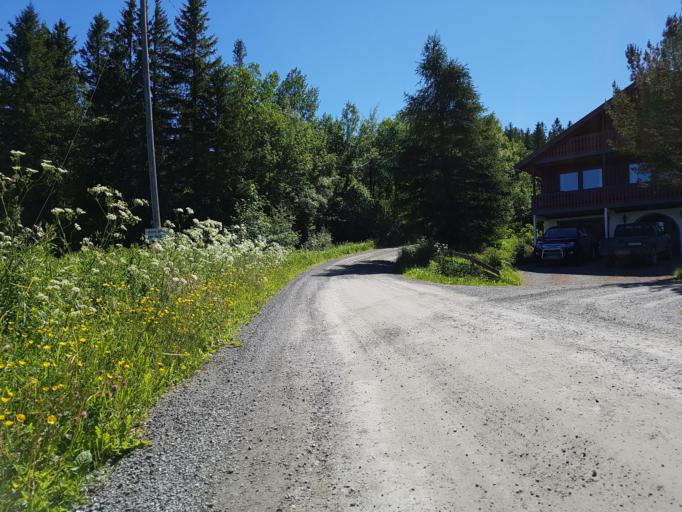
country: NO
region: Sor-Trondelag
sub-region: Skaun
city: Borsa
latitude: 63.4339
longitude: 10.1852
